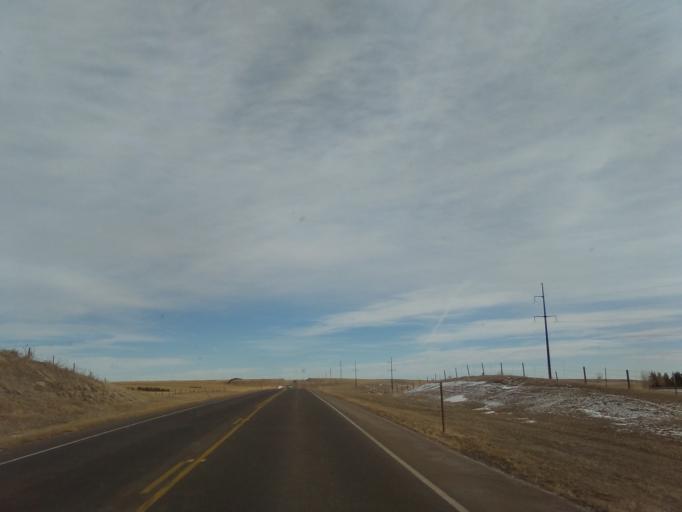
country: US
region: Wyoming
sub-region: Laramie County
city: Ranchettes
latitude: 41.3797
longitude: -104.5311
